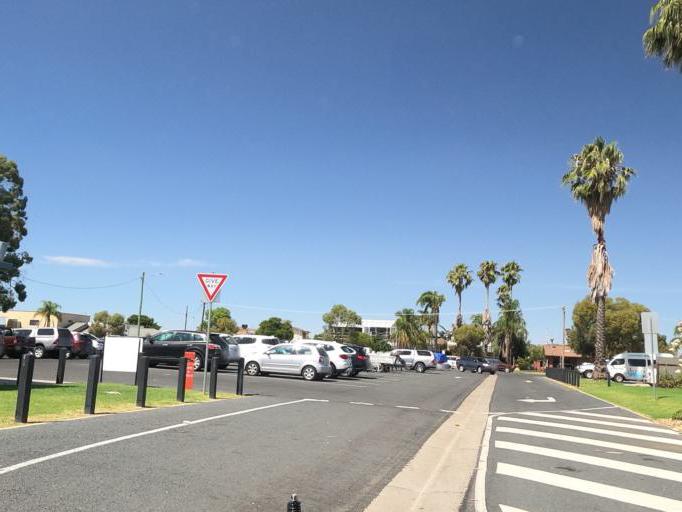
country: AU
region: New South Wales
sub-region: Corowa Shire
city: Mulwala
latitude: -35.9893
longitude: 146.0065
